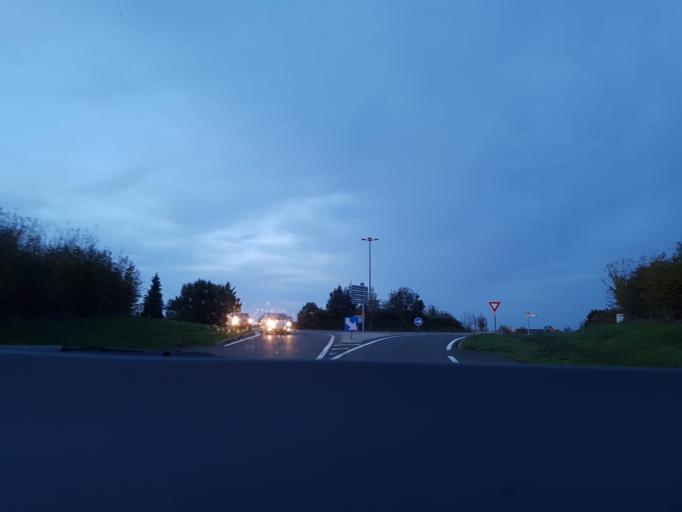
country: FR
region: Pays de la Loire
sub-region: Departement de la Mayenne
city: Montigne-le-Brillant
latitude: 48.0153
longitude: -0.8274
